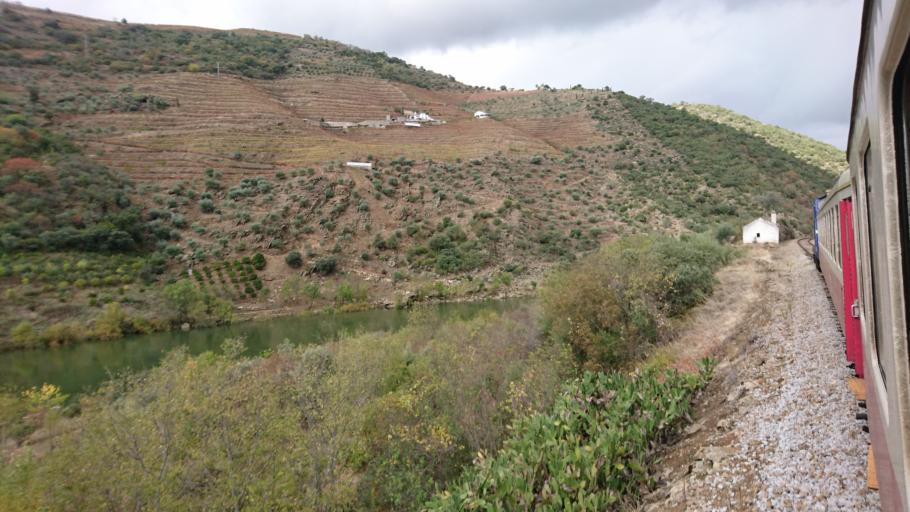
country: PT
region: Viseu
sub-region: Sao Joao da Pesqueira
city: Sao Joao da Pesqueira
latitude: 41.1838
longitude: -7.3844
